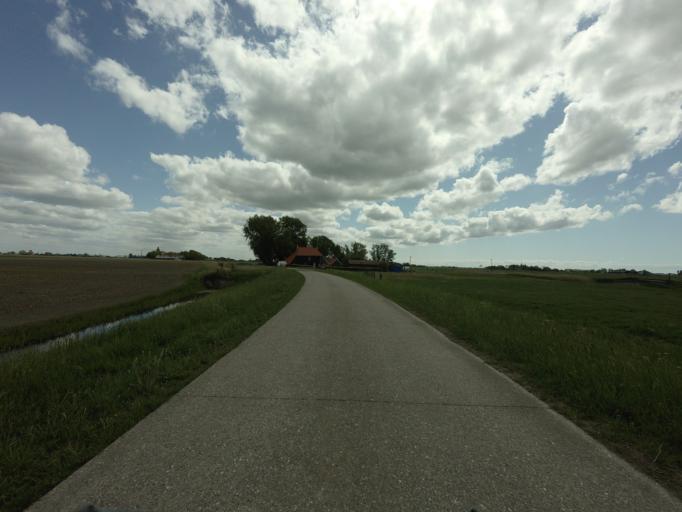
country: NL
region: Friesland
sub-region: Gemeente Littenseradiel
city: Wommels
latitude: 53.1177
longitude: 5.5506
